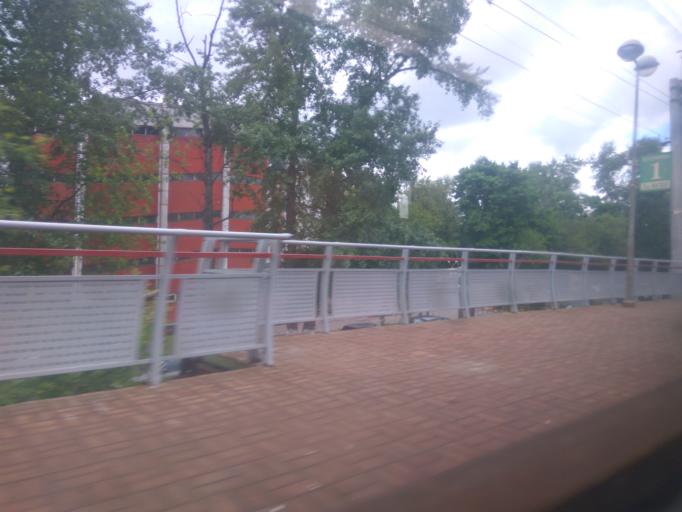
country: RU
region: Moscow
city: Lefortovo
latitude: 55.7623
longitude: 37.7204
